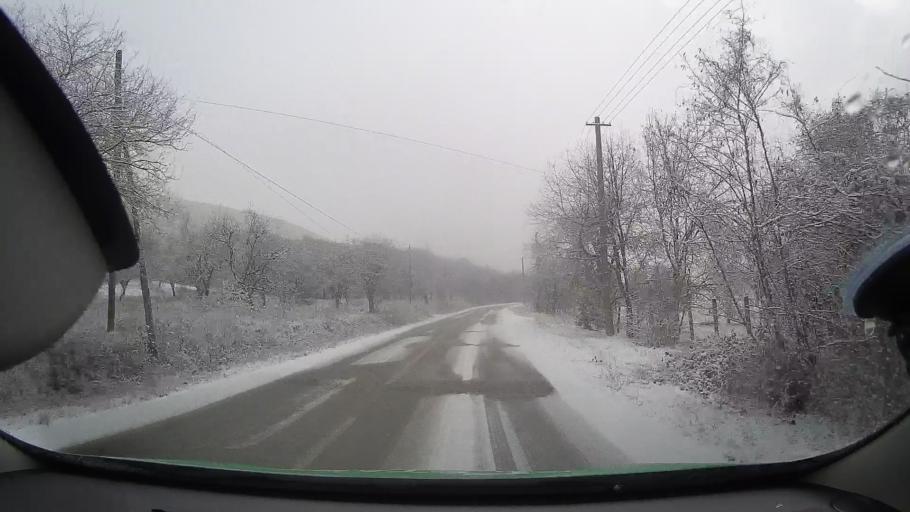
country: RO
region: Alba
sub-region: Municipiul Aiud
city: Aiudul de Sus
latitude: 46.3381
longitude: 23.6696
